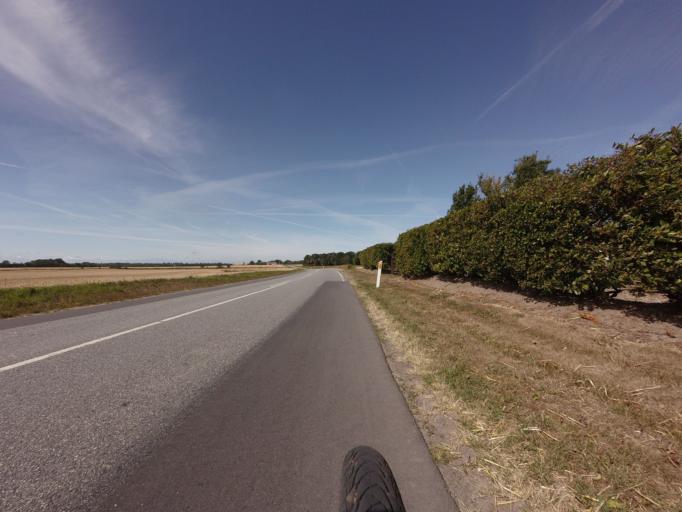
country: DK
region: North Denmark
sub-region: Hjorring Kommune
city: Vra
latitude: 57.3313
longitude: 9.8196
